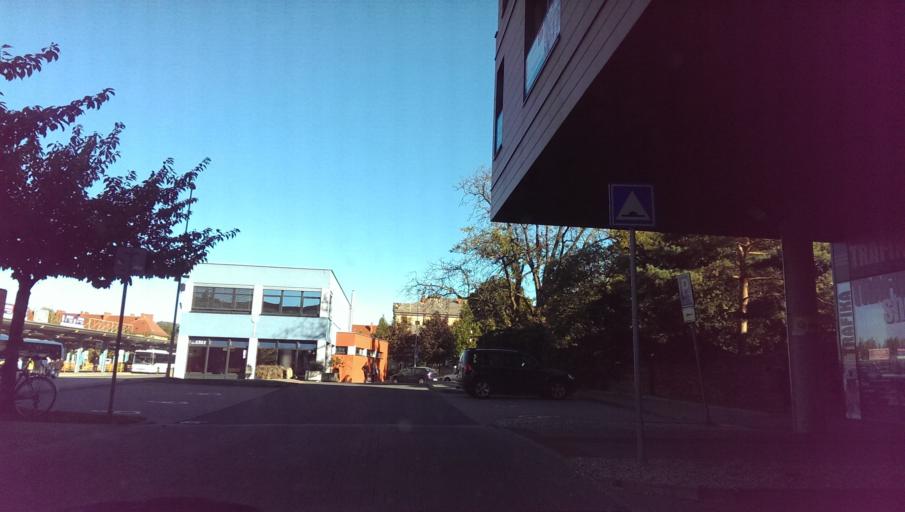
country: CZ
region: Zlin
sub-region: Okres Uherske Hradiste
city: Uherske Hradiste
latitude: 49.0696
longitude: 17.4637
